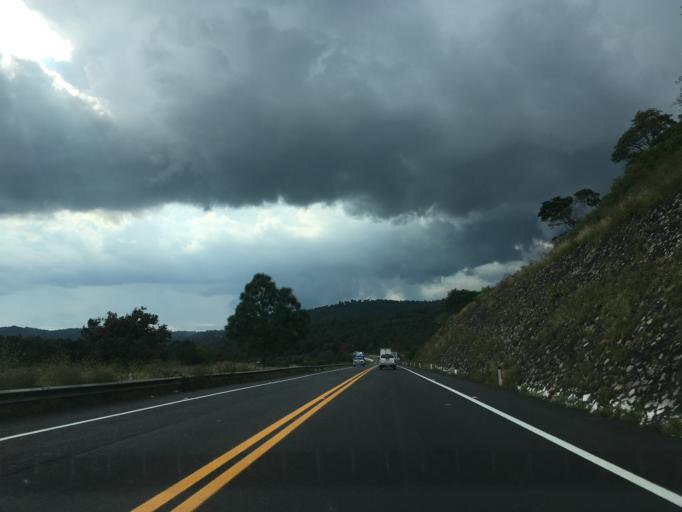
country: MX
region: Michoacan
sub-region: Ziracuaretiro
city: Patuan
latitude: 19.4161
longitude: -101.9528
